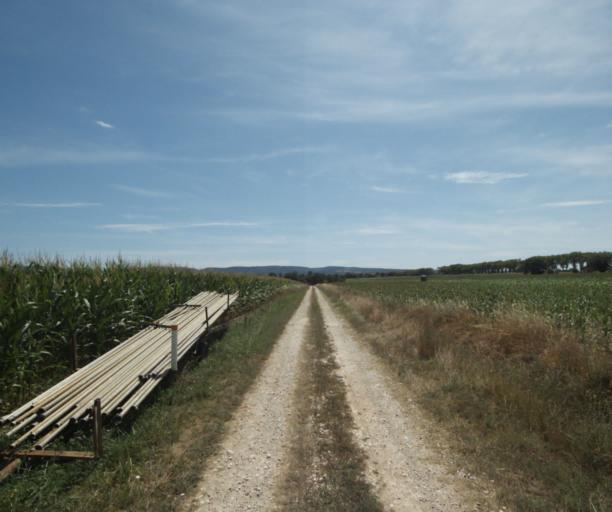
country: FR
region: Midi-Pyrenees
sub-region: Departement de la Haute-Garonne
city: Revel
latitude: 43.4986
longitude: 2.0157
